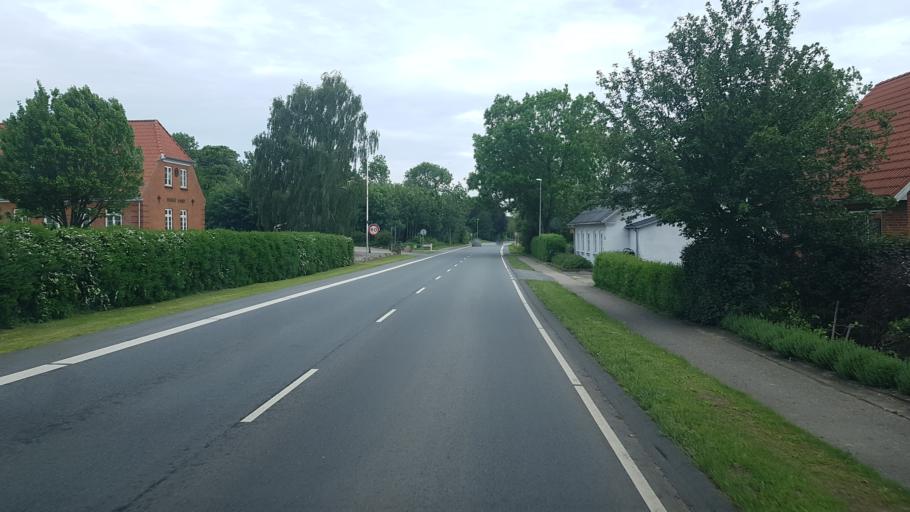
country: DK
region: South Denmark
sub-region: Vejen Kommune
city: Brorup
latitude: 55.4302
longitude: 9.0133
